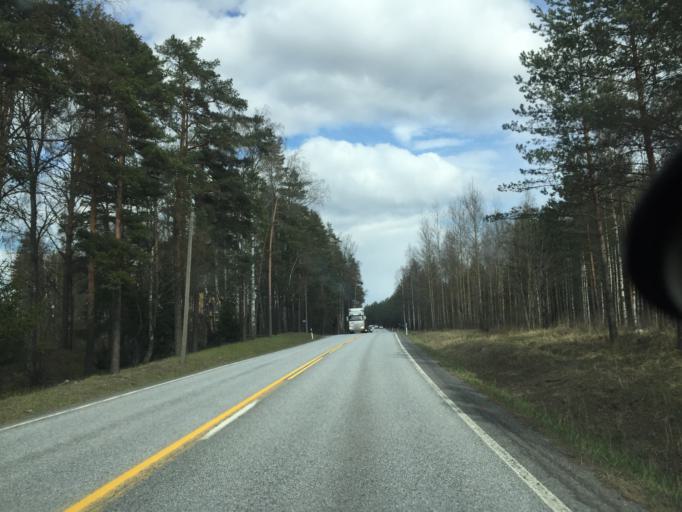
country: FI
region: Uusimaa
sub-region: Raaseporin
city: Inga
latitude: 60.1521
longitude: 23.9070
